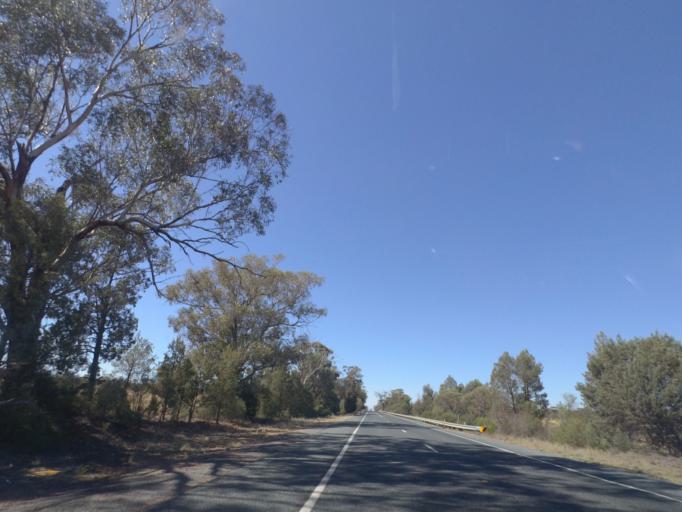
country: AU
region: New South Wales
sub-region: Bland
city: West Wyalong
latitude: -34.1633
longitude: 147.1164
